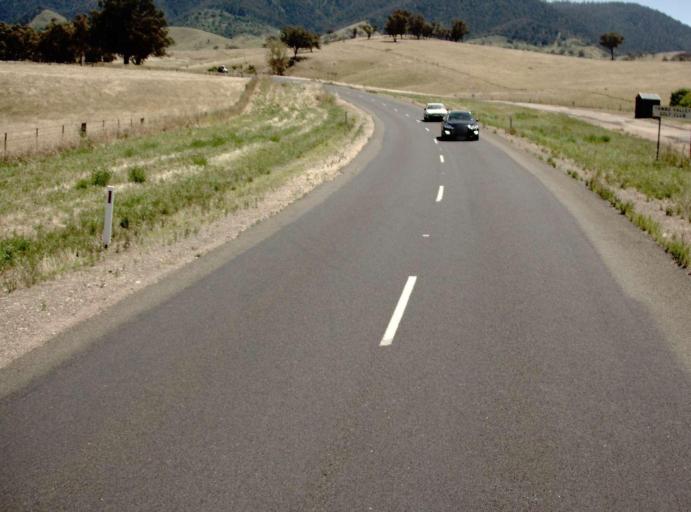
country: AU
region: Victoria
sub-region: East Gippsland
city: Bairnsdale
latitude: -37.1927
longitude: 147.7242
